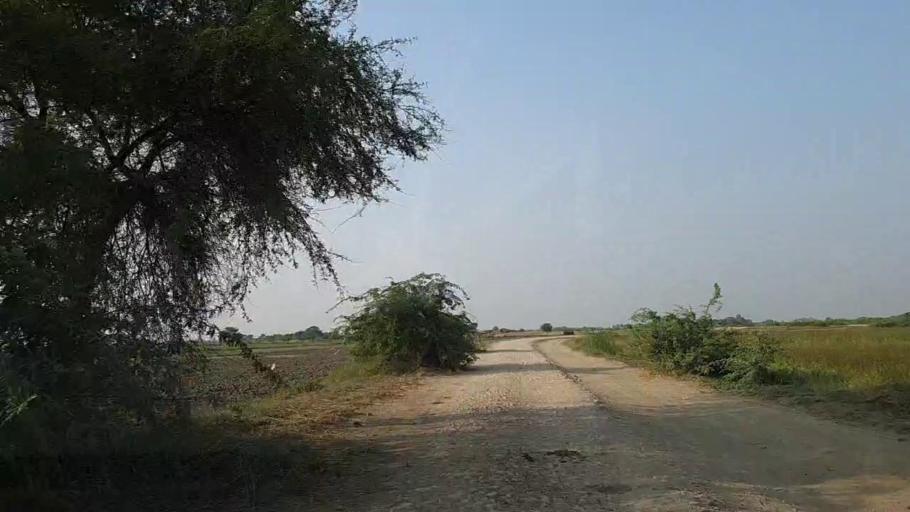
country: PK
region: Sindh
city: Mirpur Sakro
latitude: 24.6366
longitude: 67.7678
